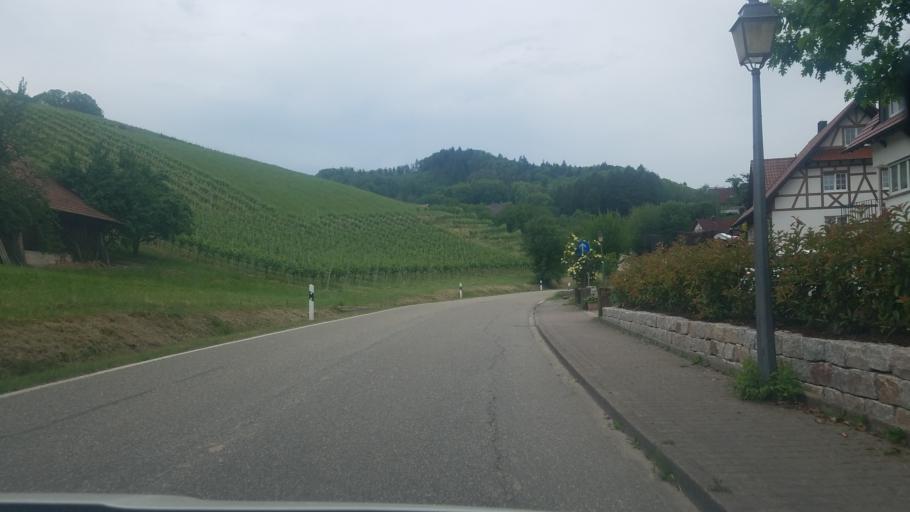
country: DE
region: Baden-Wuerttemberg
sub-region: Freiburg Region
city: Sasbachwalden
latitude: 48.6177
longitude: 8.1149
